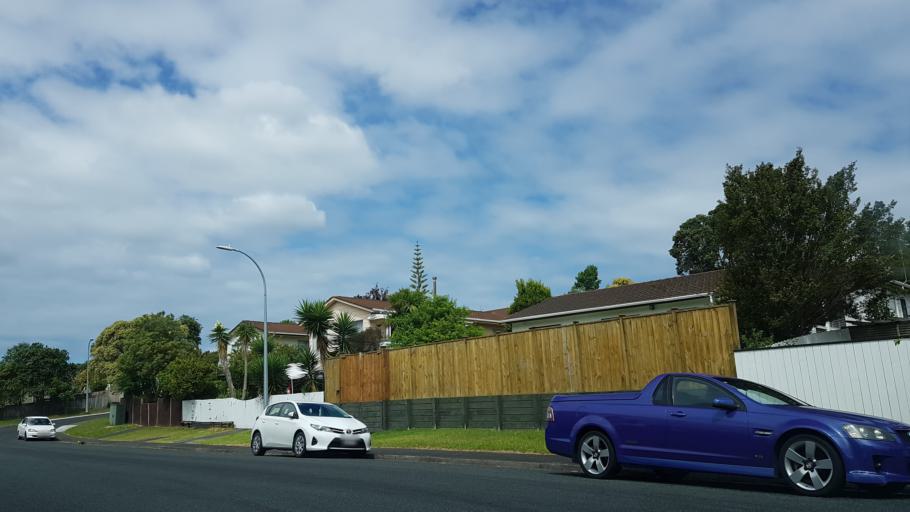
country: NZ
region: Auckland
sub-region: Auckland
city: North Shore
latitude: -36.7743
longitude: 174.7016
